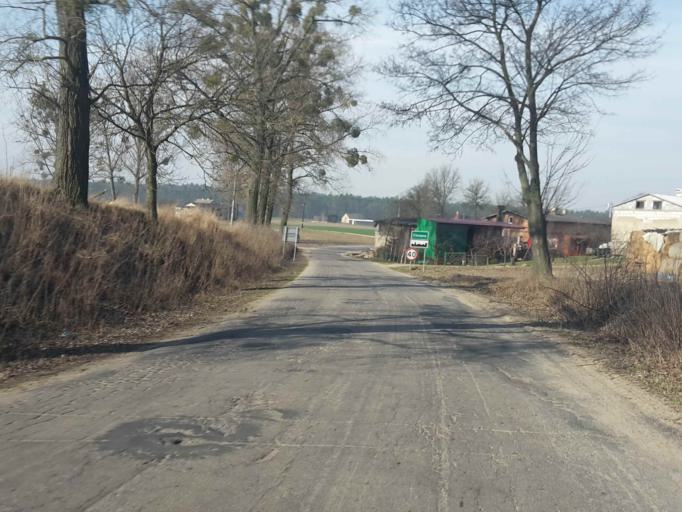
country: PL
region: Kujawsko-Pomorskie
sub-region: Powiat rypinski
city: Wapielsk
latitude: 53.2080
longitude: 19.2058
